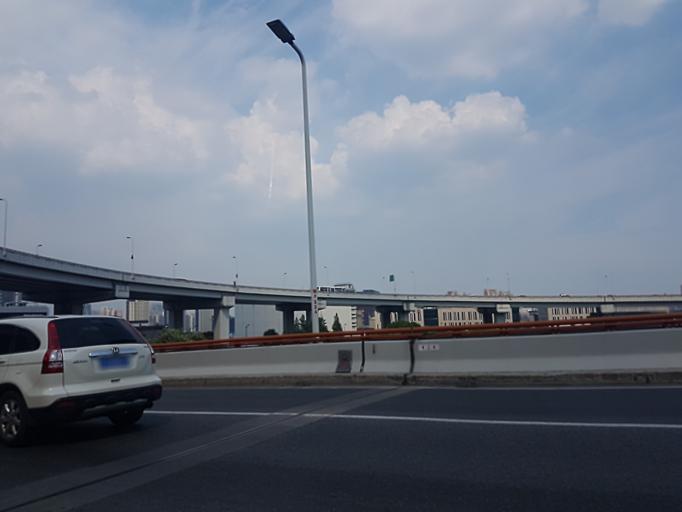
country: CN
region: Shanghai Shi
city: Luwan
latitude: 31.2105
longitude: 121.4966
